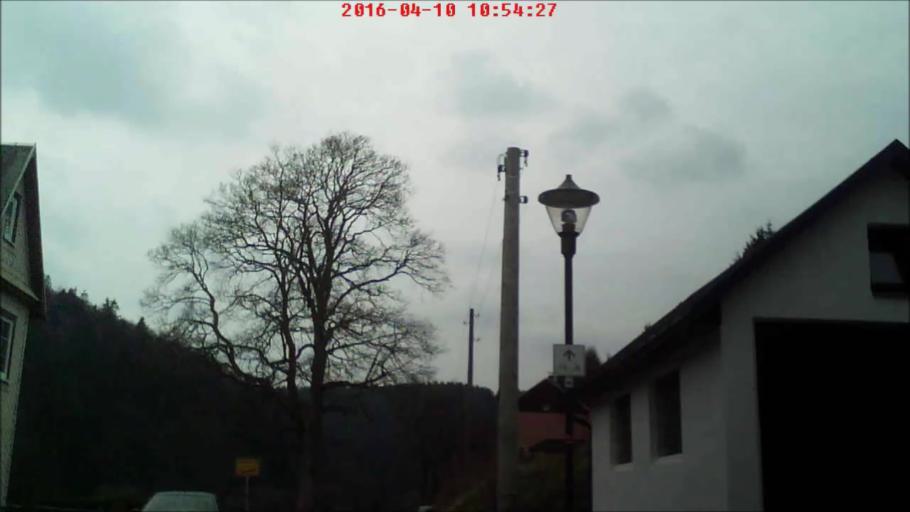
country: DE
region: Thuringia
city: Stutzerbach
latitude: 50.6299
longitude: 10.8590
